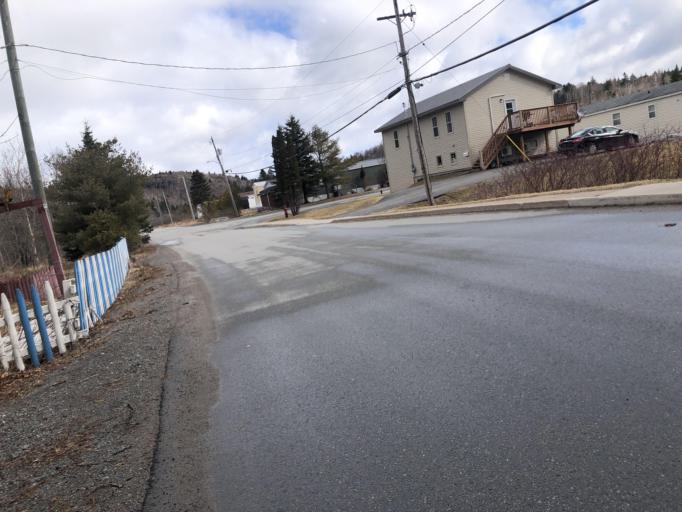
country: CA
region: New Brunswick
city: Saint John
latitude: 45.3239
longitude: -66.0131
